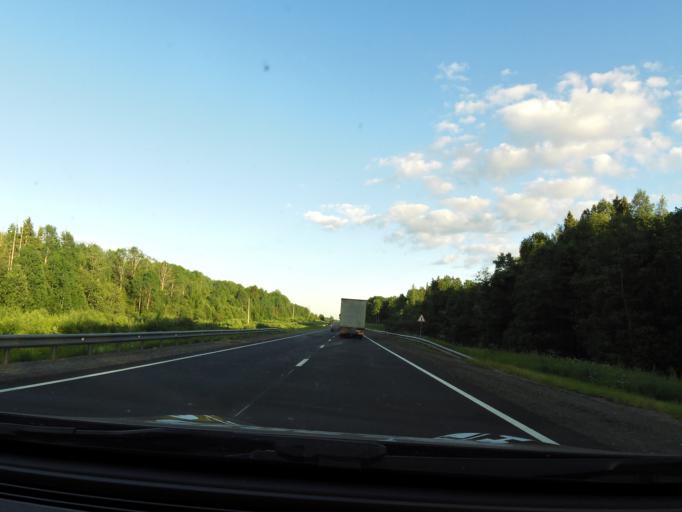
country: RU
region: Vologda
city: Gryazovets
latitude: 58.9919
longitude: 40.1357
